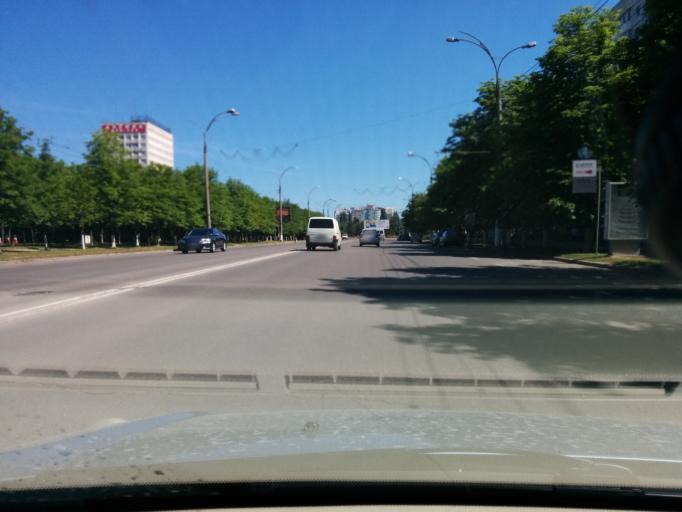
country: MD
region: Chisinau
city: Stauceni
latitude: 47.0566
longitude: 28.8661
